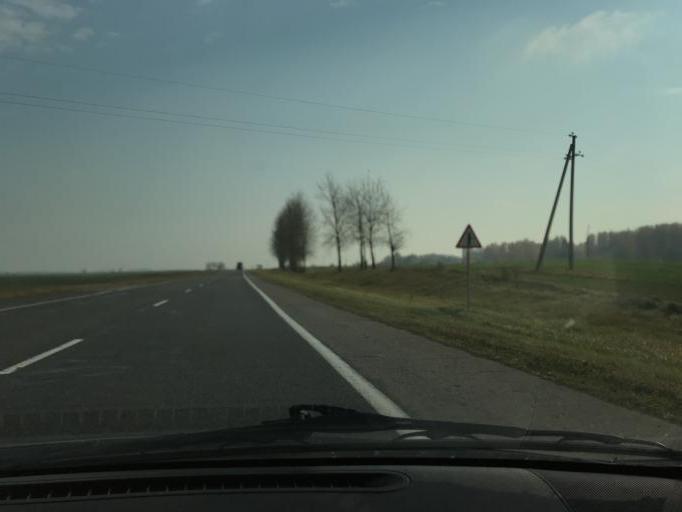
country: BY
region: Vitebsk
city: Chashniki
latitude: 55.0170
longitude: 29.0410
